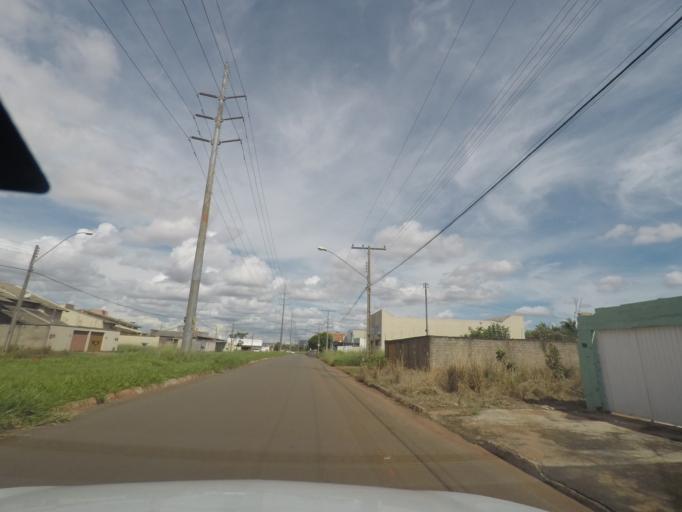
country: BR
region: Goias
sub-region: Goiania
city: Goiania
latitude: -16.7174
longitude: -49.3455
